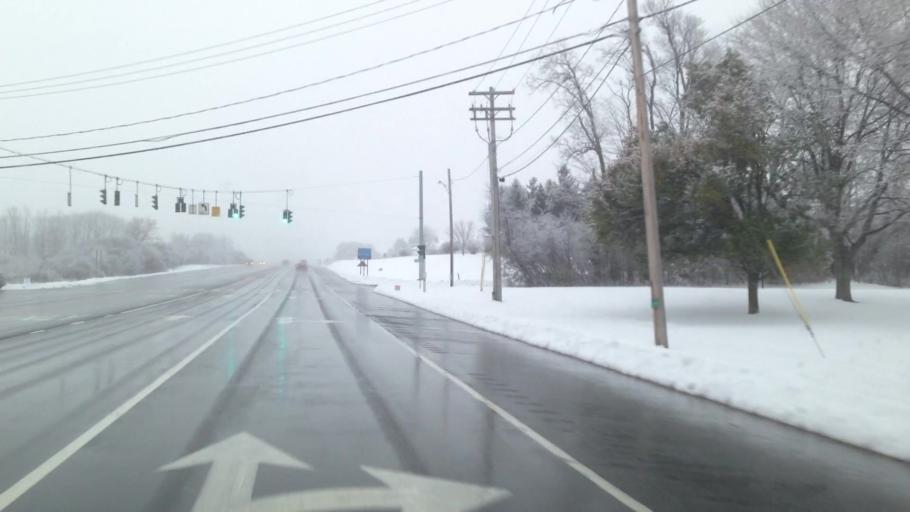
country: US
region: New York
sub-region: Onondaga County
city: Camillus
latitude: 43.0362
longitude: -76.3355
